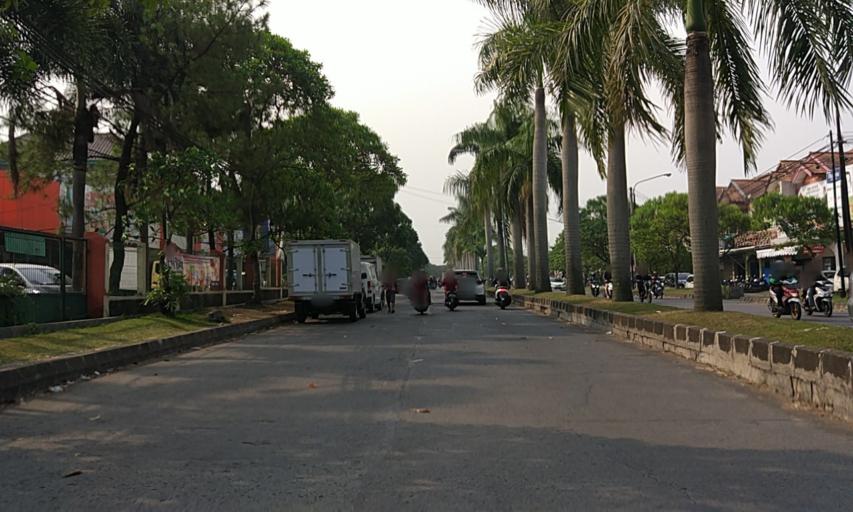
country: ID
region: West Java
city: Margahayukencana
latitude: -6.9579
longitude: 107.5611
